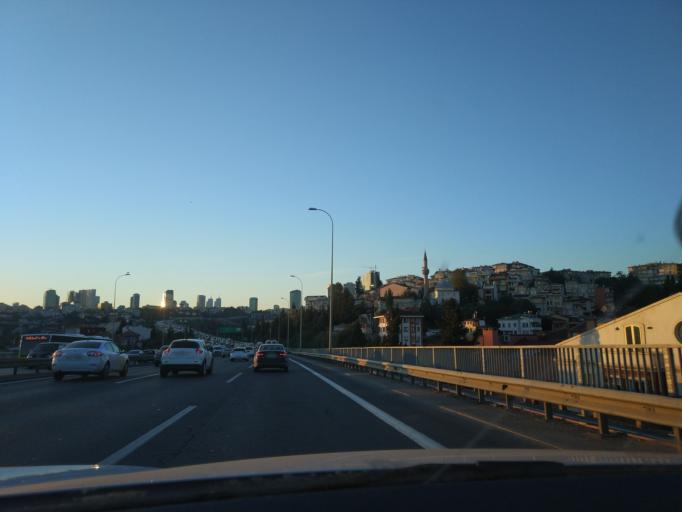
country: TR
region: Istanbul
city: UEskuedar
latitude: 41.0519
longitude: 29.0279
